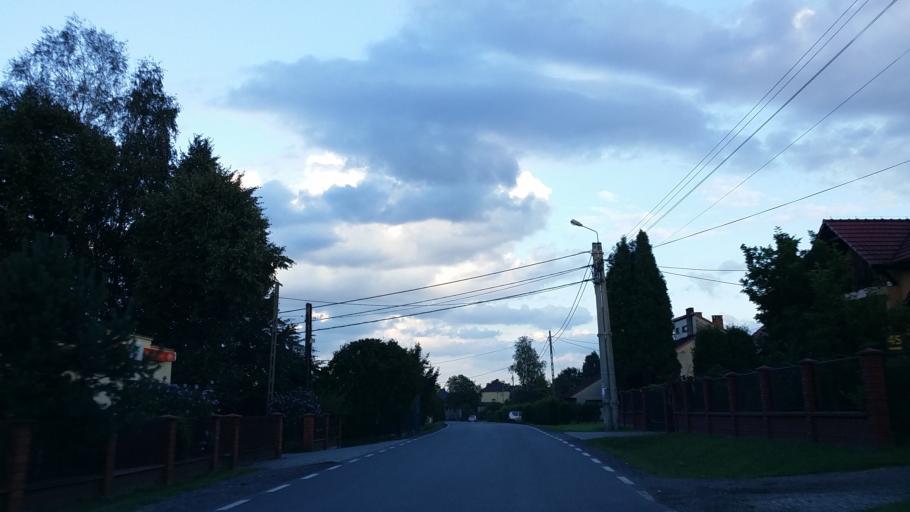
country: PL
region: Lesser Poland Voivodeship
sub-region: Powiat oswiecimski
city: Osiek
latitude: 49.9667
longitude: 19.2646
